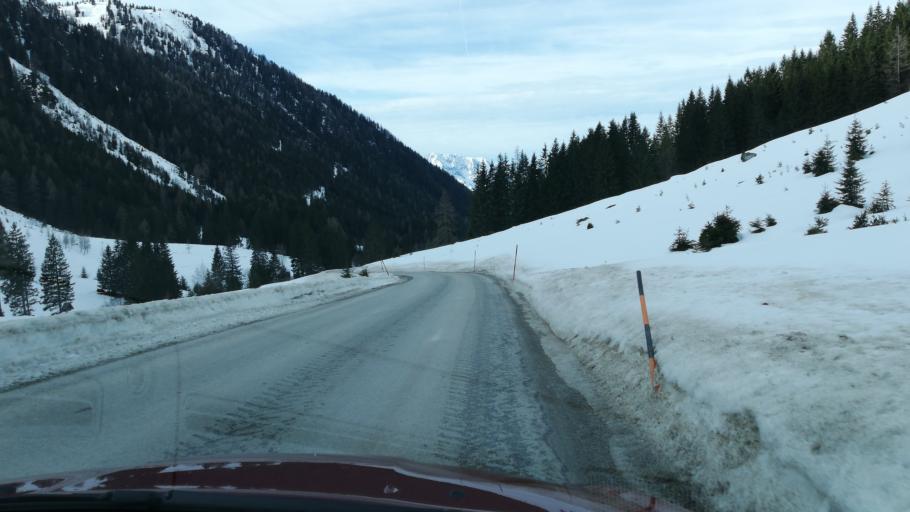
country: AT
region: Styria
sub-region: Politischer Bezirk Liezen
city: Donnersbach
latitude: 47.4138
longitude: 14.1785
